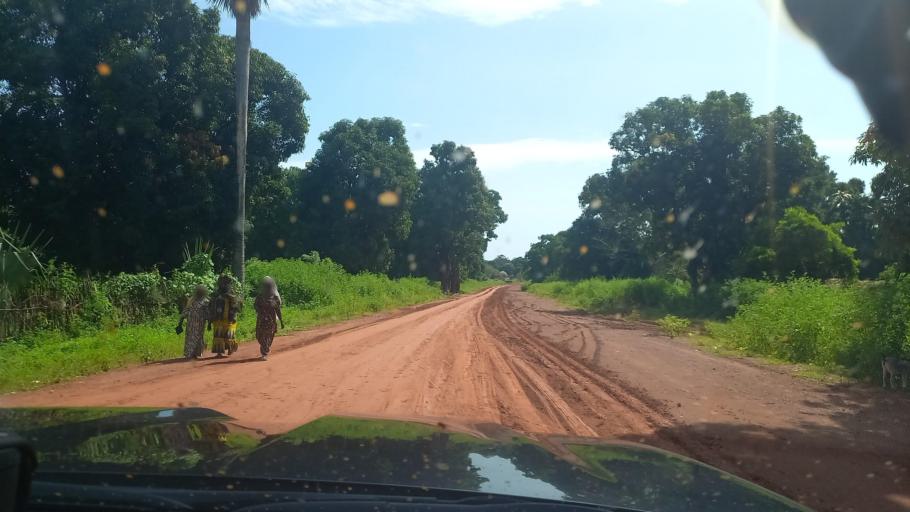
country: SN
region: Ziguinchor
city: Adeane
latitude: 12.6685
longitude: -16.0961
